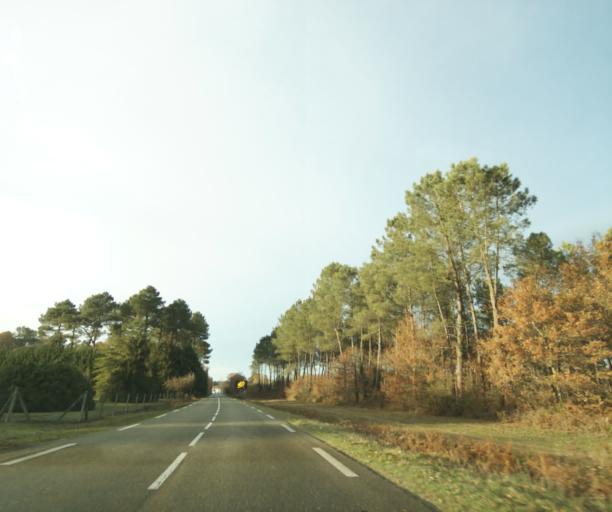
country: FR
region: Aquitaine
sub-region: Departement des Landes
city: Gabarret
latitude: 44.0622
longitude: -0.0502
